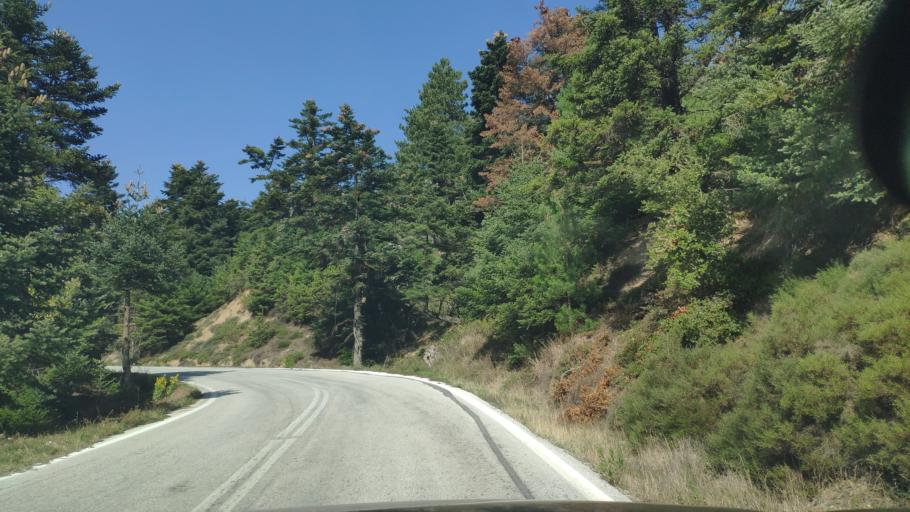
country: GR
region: West Greece
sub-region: Nomos Achaias
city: Aiyira
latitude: 37.8653
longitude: 22.3689
